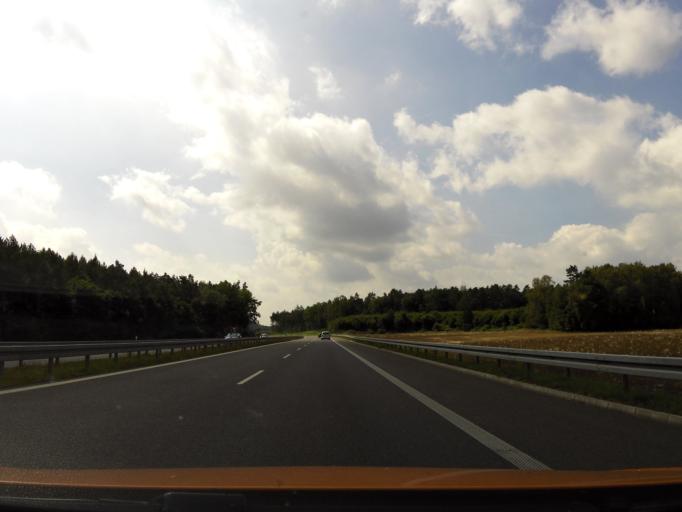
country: PL
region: West Pomeranian Voivodeship
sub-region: Powiat goleniowski
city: Nowogard
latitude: 53.6708
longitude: 15.0783
